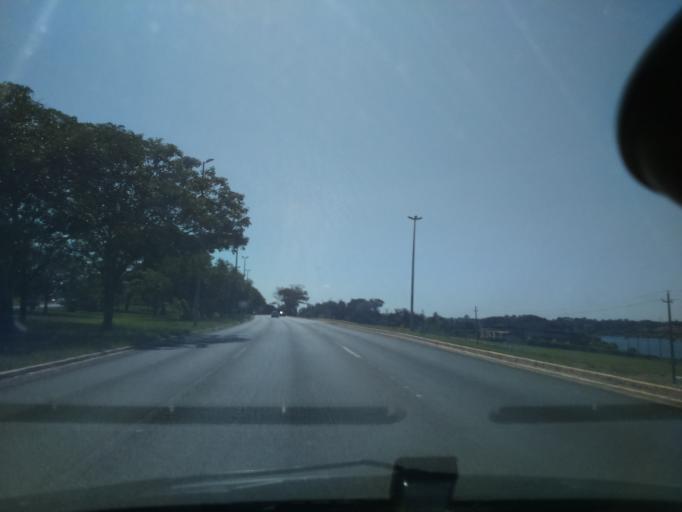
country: BR
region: Federal District
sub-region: Brasilia
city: Brasilia
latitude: -15.8338
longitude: -47.8950
